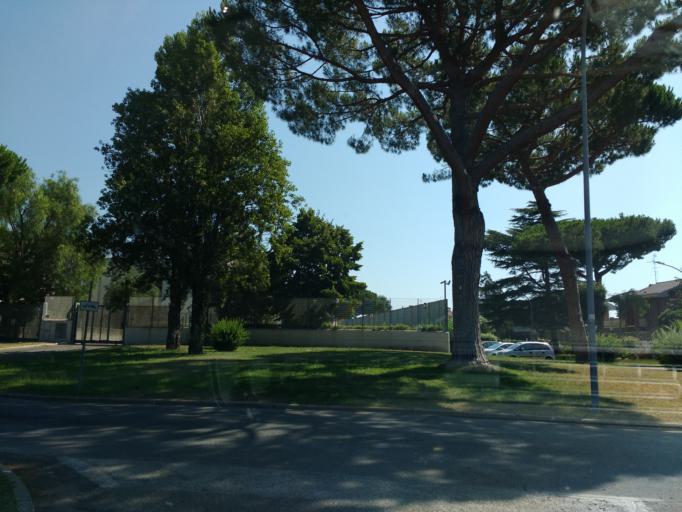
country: IT
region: Latium
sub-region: Citta metropolitana di Roma Capitale
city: Acilia-Castel Fusano-Ostia Antica
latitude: 41.7575
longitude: 12.3604
